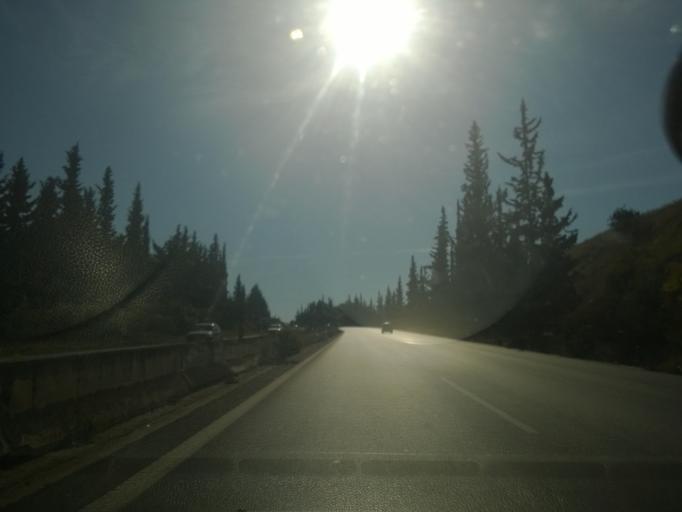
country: GR
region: Central Macedonia
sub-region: Nomos Thessalonikis
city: Neo Rysi
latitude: 40.4853
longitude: 22.9951
